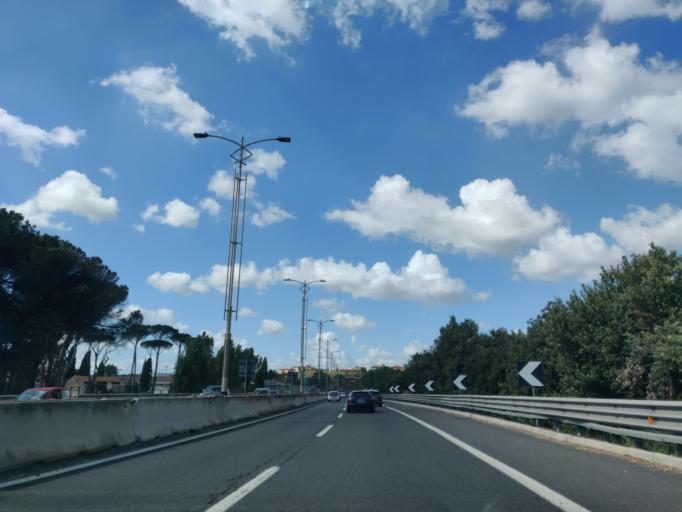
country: IT
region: Latium
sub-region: Citta metropolitana di Roma Capitale
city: Vitinia
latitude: 41.8263
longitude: 12.4200
